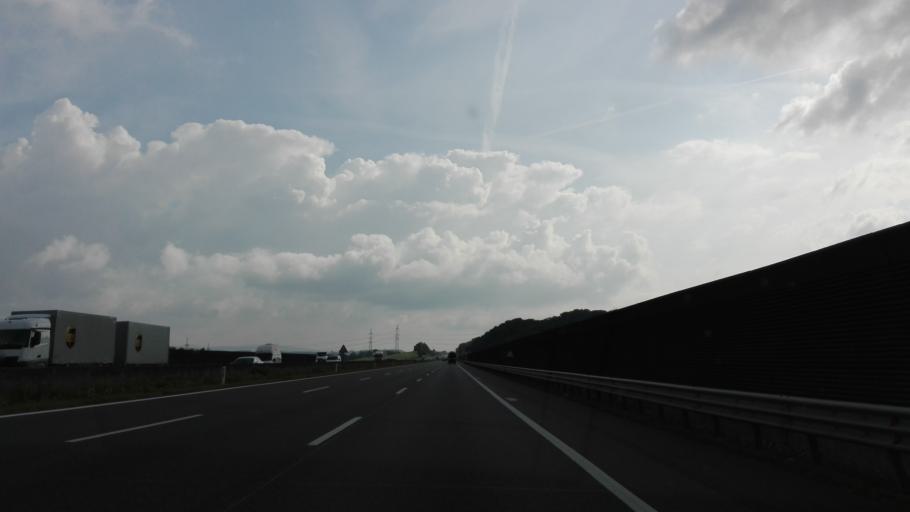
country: AT
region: Lower Austria
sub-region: Politischer Bezirk Melk
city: Ybbs an der Donau
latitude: 48.1430
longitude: 15.0742
